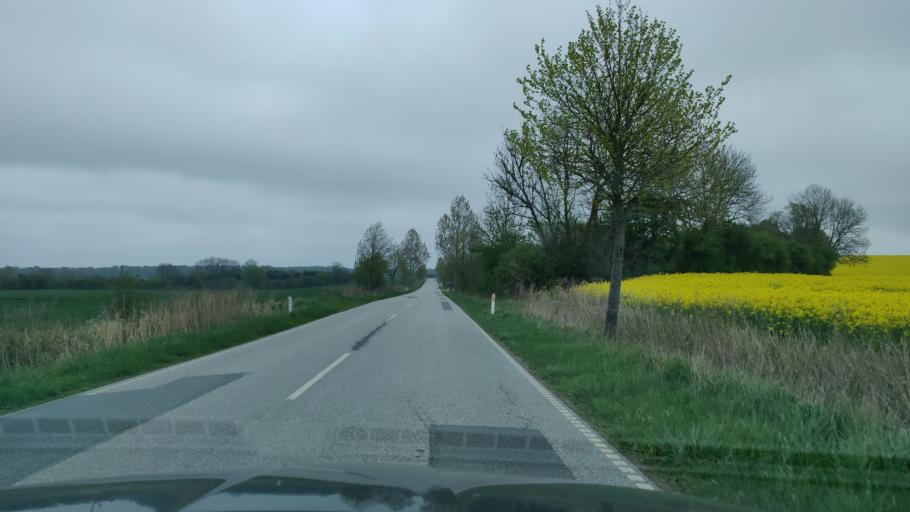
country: DK
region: South Denmark
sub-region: Sonderborg Kommune
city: Guderup
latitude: 54.9976
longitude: 9.9095
